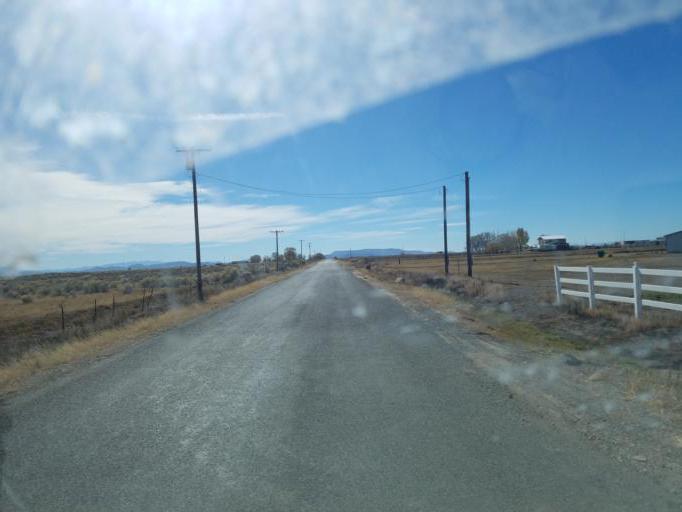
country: US
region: Colorado
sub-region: Alamosa County
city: Alamosa East
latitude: 37.4790
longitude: -105.7849
